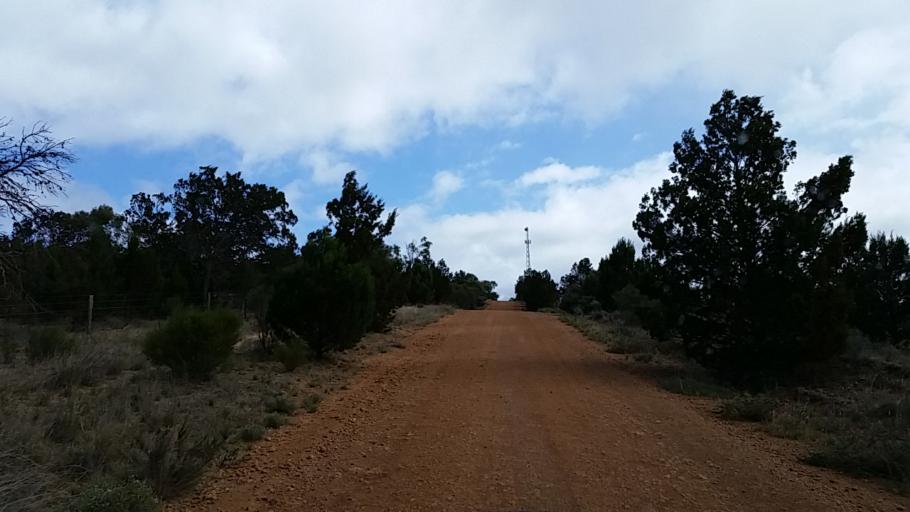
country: AU
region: South Australia
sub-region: Peterborough
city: Peterborough
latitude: -32.9630
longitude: 138.8317
